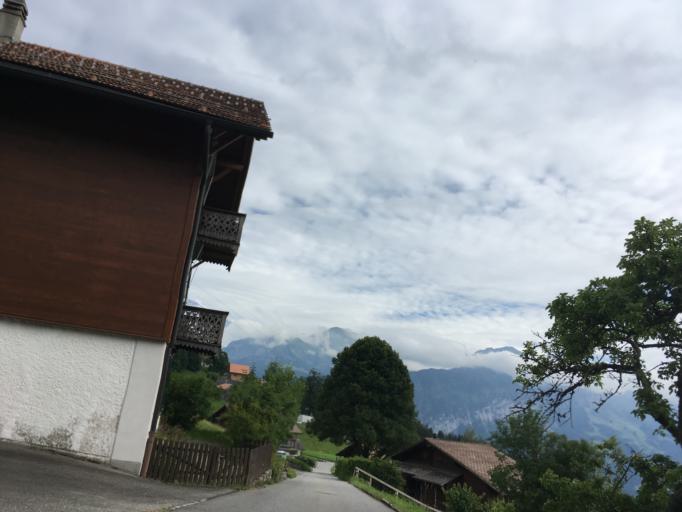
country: CH
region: Bern
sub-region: Interlaken-Oberhasli District
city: Beatenberg
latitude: 46.7036
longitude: 7.8128
